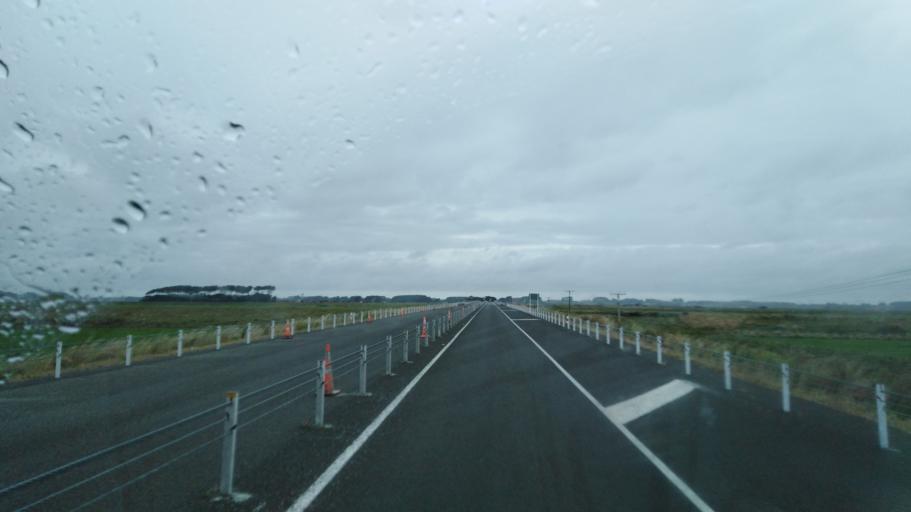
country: NZ
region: Manawatu-Wanganui
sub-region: Horowhenua District
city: Foxton
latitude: -40.5093
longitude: 175.2798
